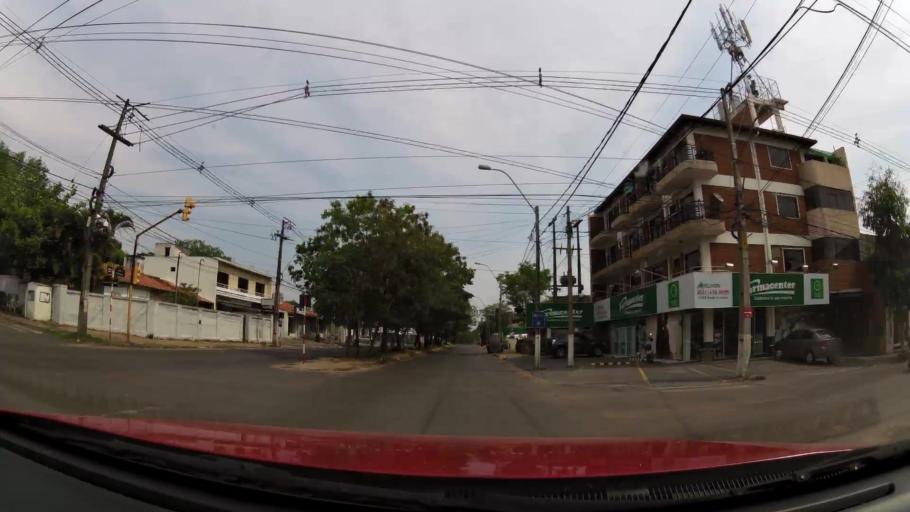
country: PY
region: Asuncion
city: Asuncion
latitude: -25.2800
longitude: -57.5709
